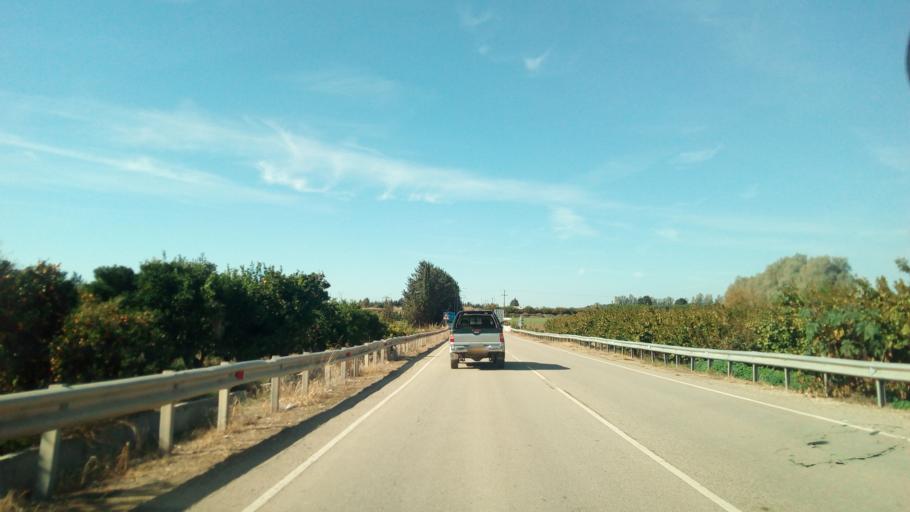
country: CY
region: Limassol
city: Pissouri
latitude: 34.7090
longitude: 32.5650
